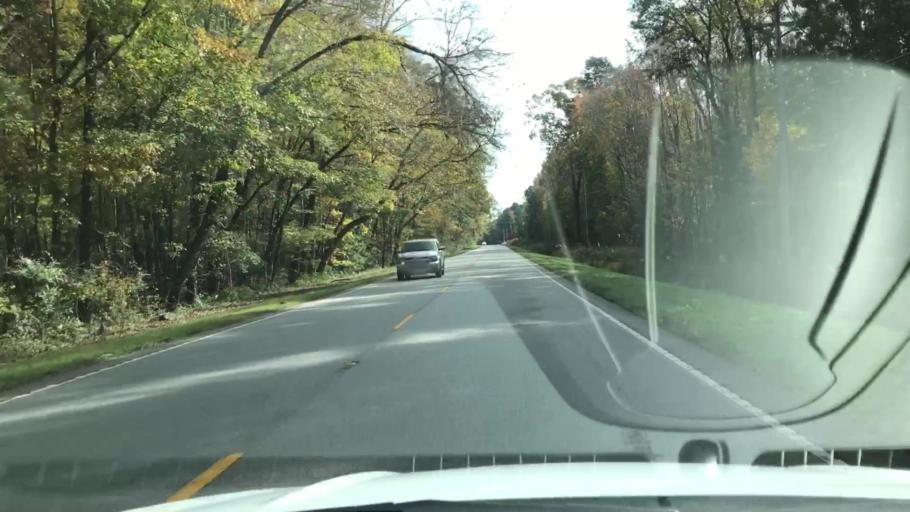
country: US
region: South Carolina
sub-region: Colleton County
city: Walterboro
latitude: 32.8034
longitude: -80.5089
